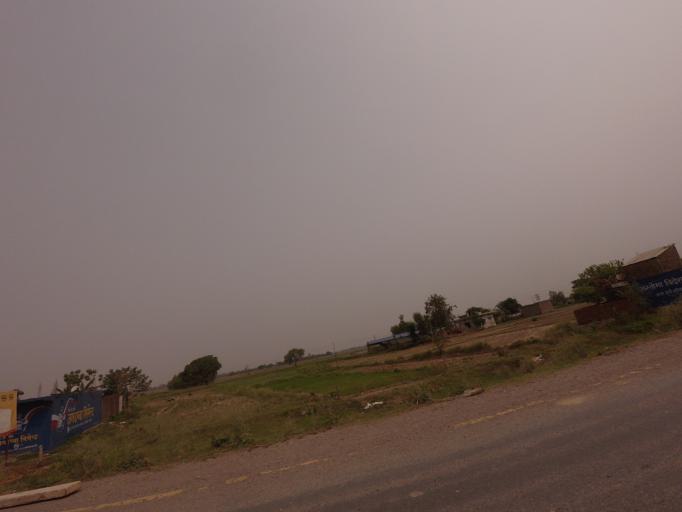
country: NP
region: Western Region
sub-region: Lumbini Zone
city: Bhairahawa
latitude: 27.5091
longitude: 83.3878
